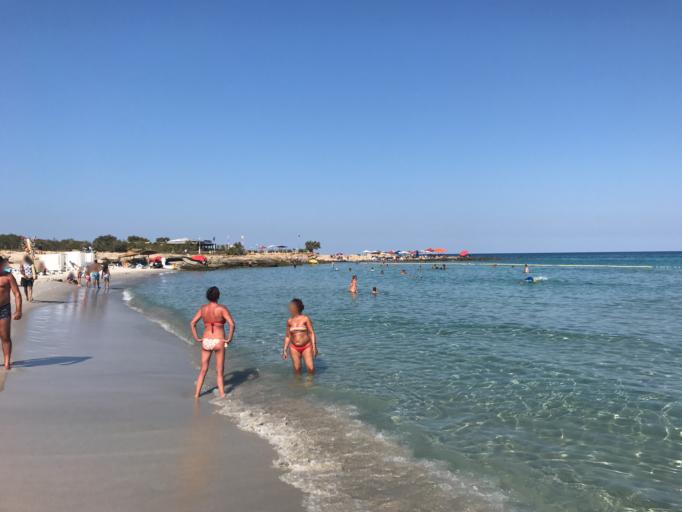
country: TN
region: Nabul
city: Qulaybiyah
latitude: 36.8544
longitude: 11.1275
